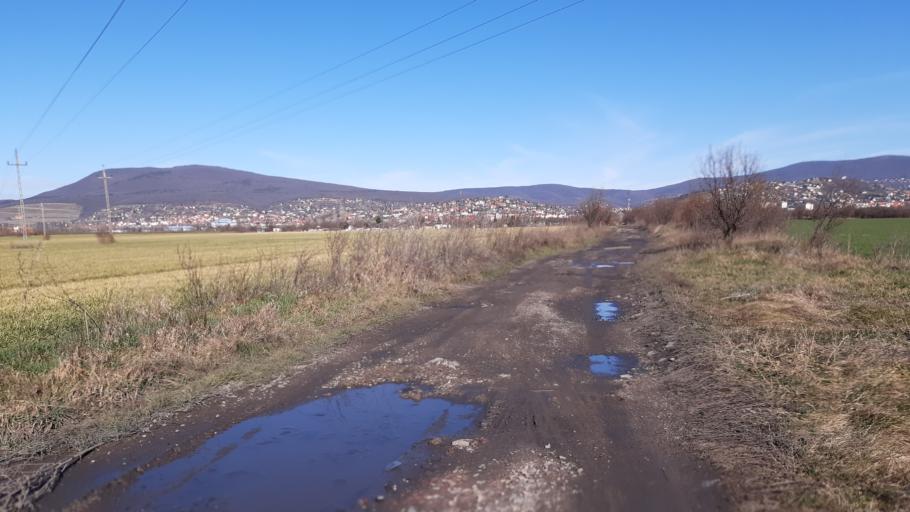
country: HU
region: Baranya
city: Pellerd
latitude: 46.0512
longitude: 18.1881
